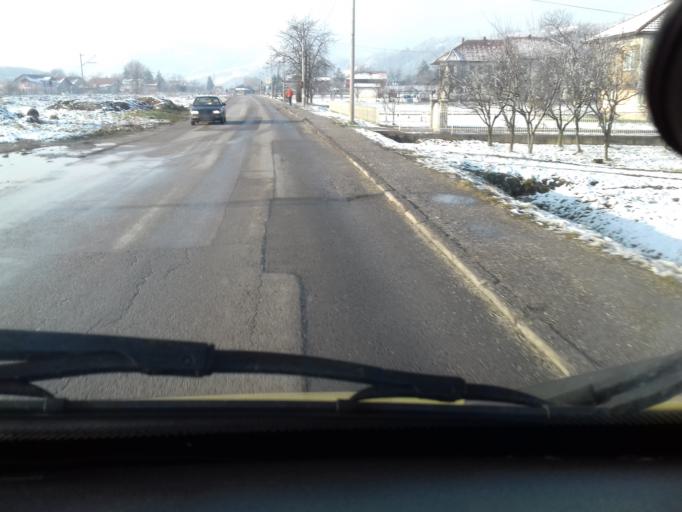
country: BA
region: Federation of Bosnia and Herzegovina
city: Mahala
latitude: 43.9864
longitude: 18.2358
